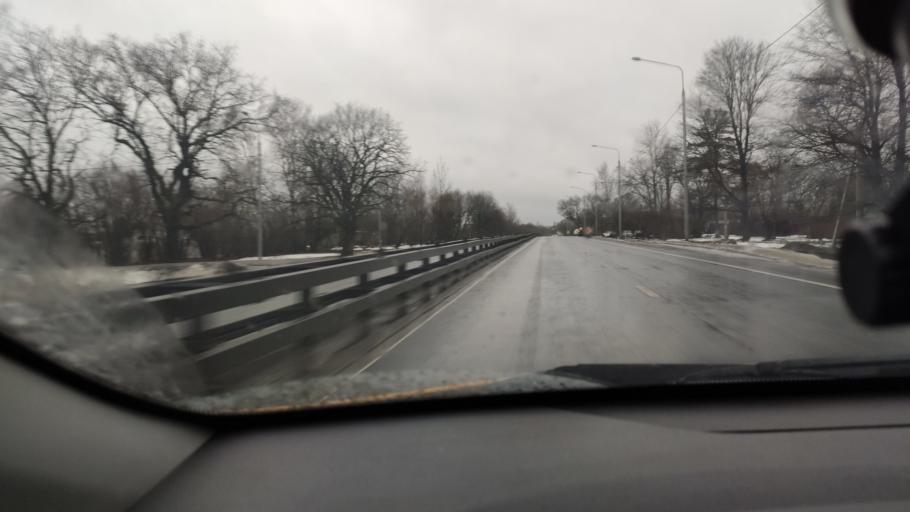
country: RU
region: Moskovskaya
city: Troitsk
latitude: 55.3068
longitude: 37.2230
